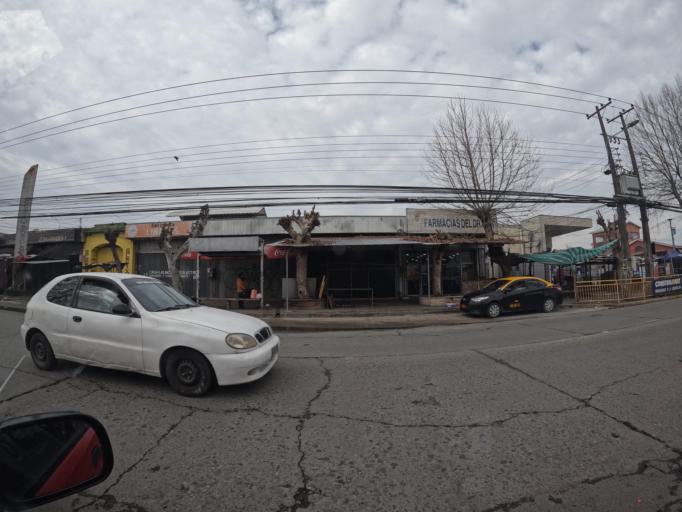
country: CL
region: Maule
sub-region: Provincia de Linares
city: Linares
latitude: -35.8463
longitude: -71.5892
